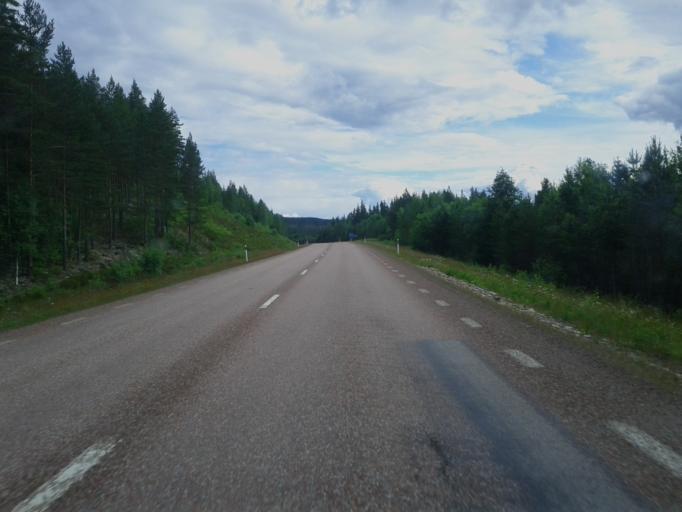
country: SE
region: Dalarna
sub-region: Rattviks Kommun
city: Raettvik
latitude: 60.7977
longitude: 15.2712
